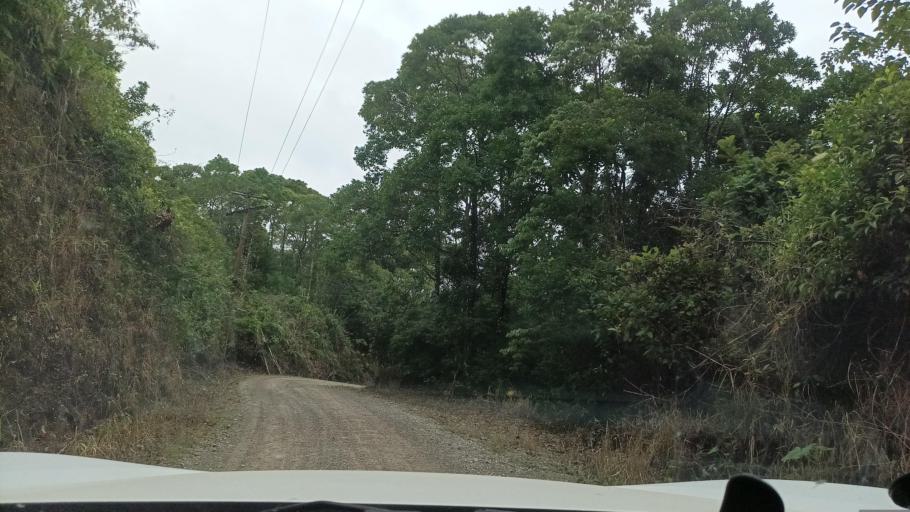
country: MX
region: Veracruz
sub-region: Uxpanapa
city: Poblado 10
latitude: 17.4200
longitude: -94.4160
